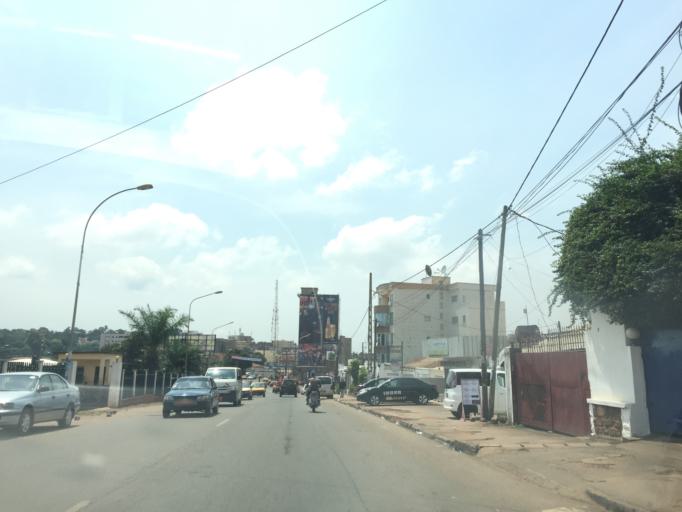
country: CM
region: Centre
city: Yaounde
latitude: 3.8693
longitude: 11.5234
